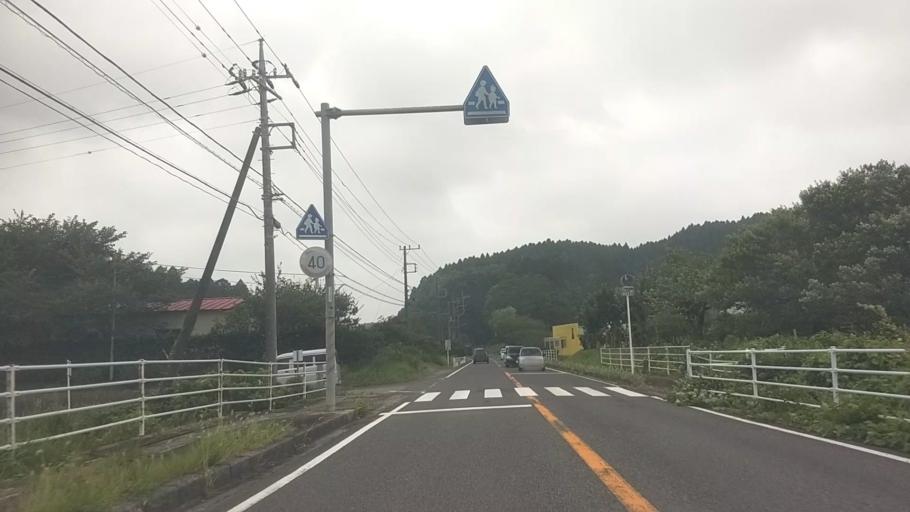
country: JP
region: Chiba
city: Ohara
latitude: 35.2640
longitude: 140.3472
